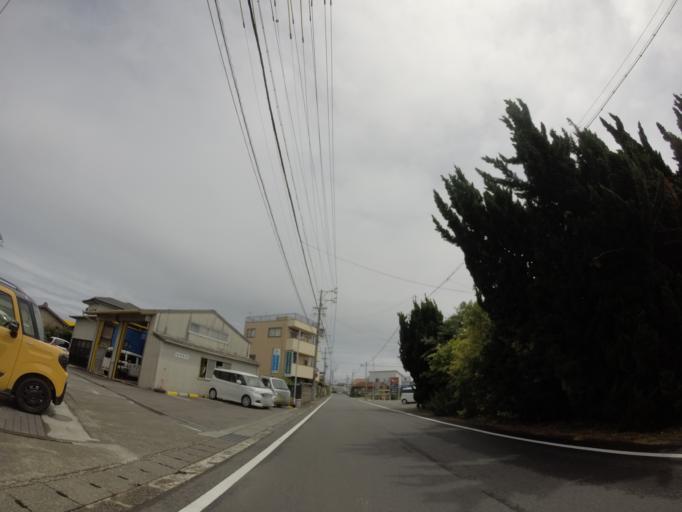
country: JP
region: Shizuoka
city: Oyama
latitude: 34.6120
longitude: 138.2018
